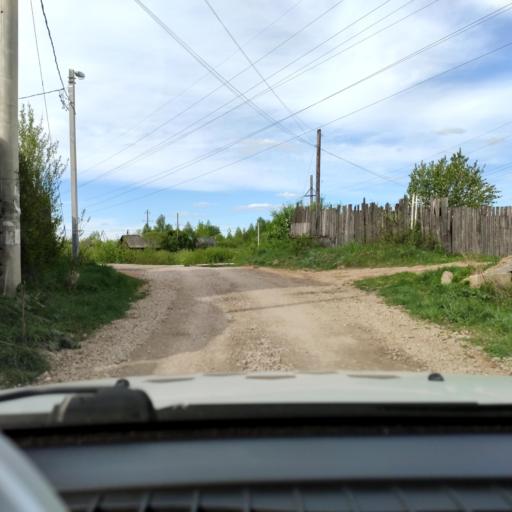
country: RU
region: Perm
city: Kondratovo
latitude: 58.0030
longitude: 56.1010
